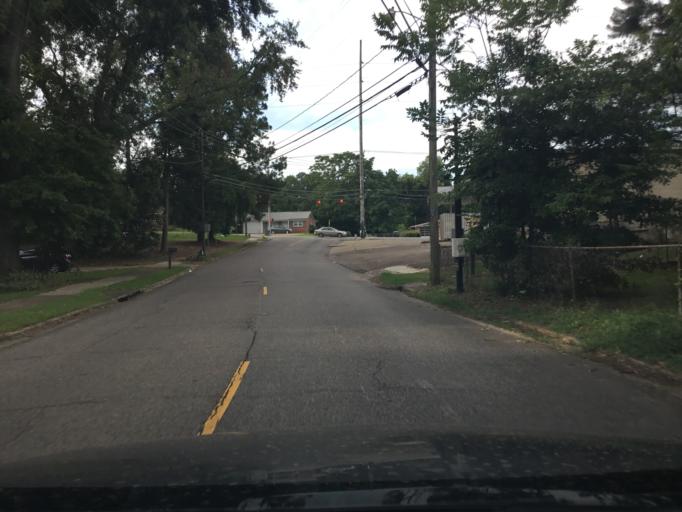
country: US
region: Alabama
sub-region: Montgomery County
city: Montgomery
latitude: 32.3679
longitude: -86.2554
